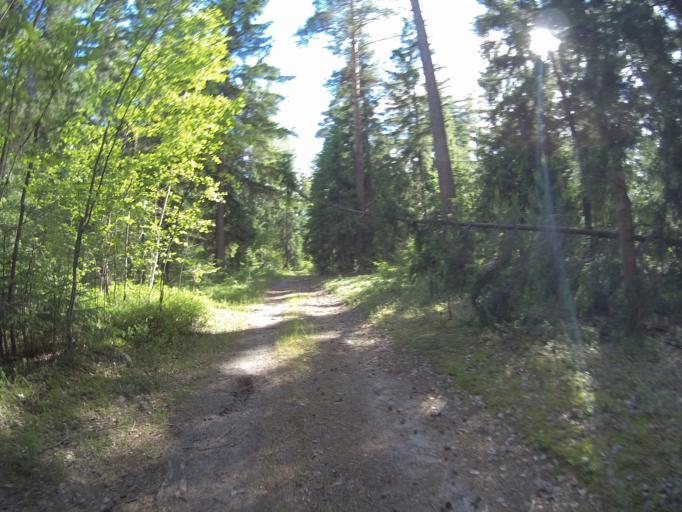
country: RU
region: Vladimir
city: Bogolyubovo
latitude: 56.0970
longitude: 40.5481
